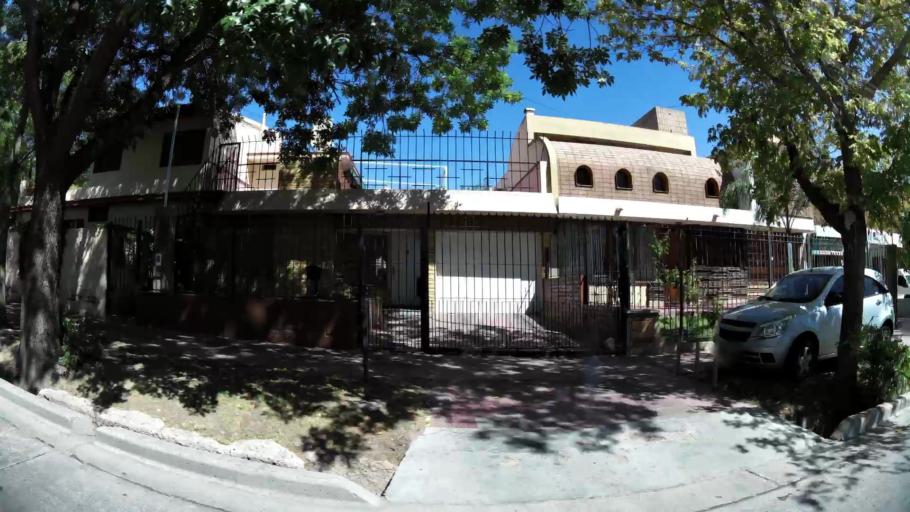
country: AR
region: Mendoza
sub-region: Departamento de Godoy Cruz
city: Godoy Cruz
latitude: -32.9409
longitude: -68.8581
